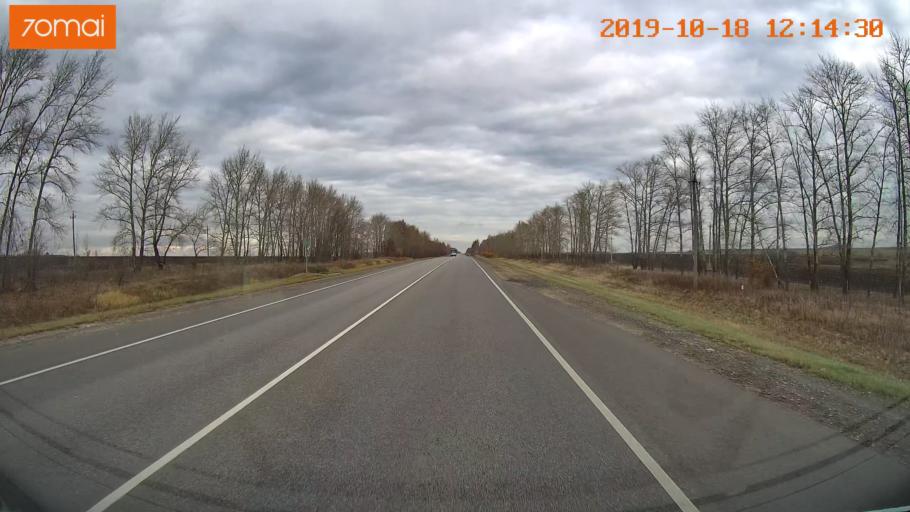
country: RU
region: Rjazan
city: Zakharovo
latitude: 54.4316
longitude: 39.3843
